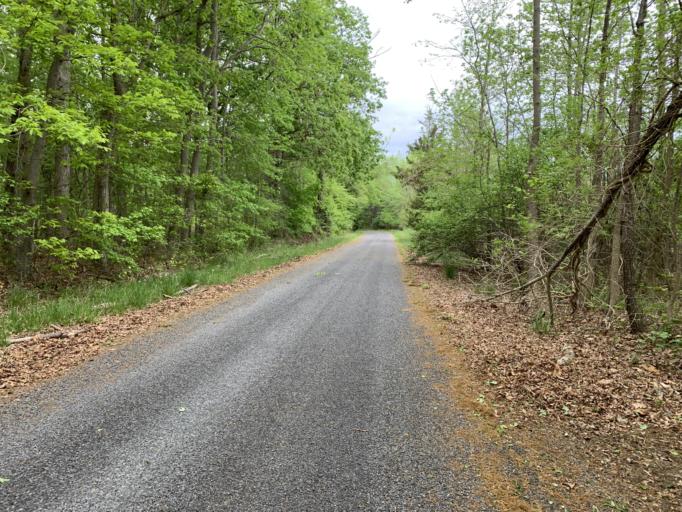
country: US
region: Delaware
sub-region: Kent County
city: Smyrna
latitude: 39.3368
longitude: -75.5244
